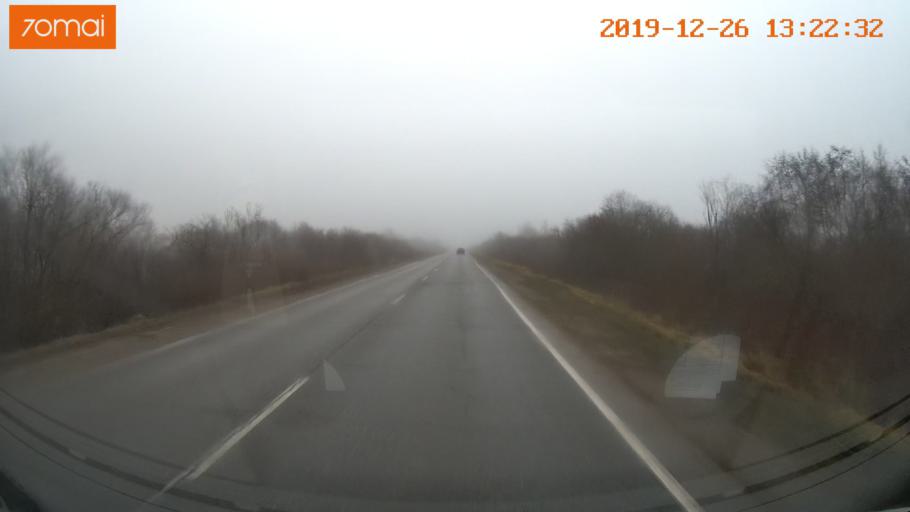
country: RU
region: Vologda
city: Cherepovets
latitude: 58.9003
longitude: 38.1738
